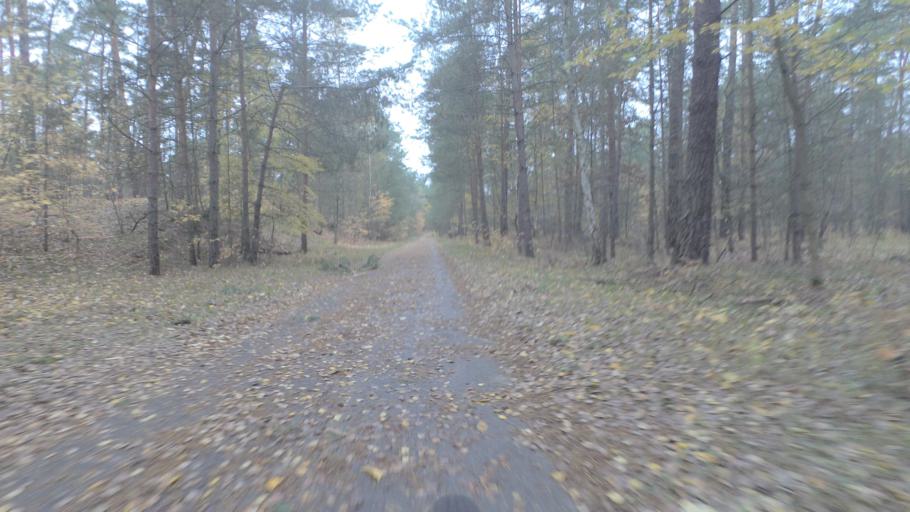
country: DE
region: Brandenburg
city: Rangsdorf
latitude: 52.3166
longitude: 13.4071
